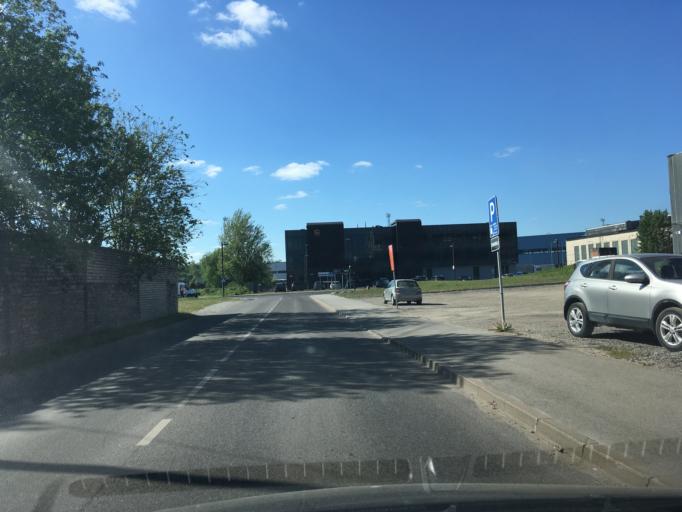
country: EE
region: Harju
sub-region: Tallinna linn
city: Tallinn
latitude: 59.4211
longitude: 24.8110
